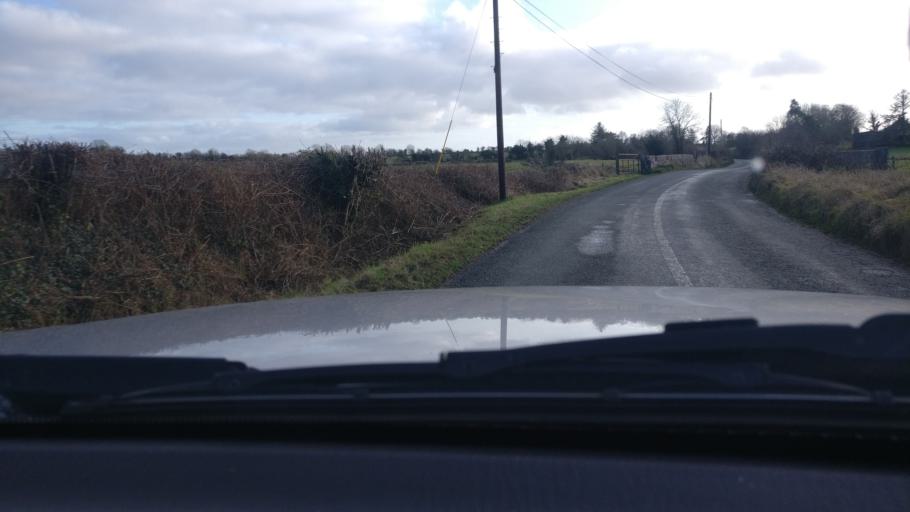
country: IE
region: Connaught
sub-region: County Galway
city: Ballinasloe
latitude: 53.2266
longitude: -8.2931
